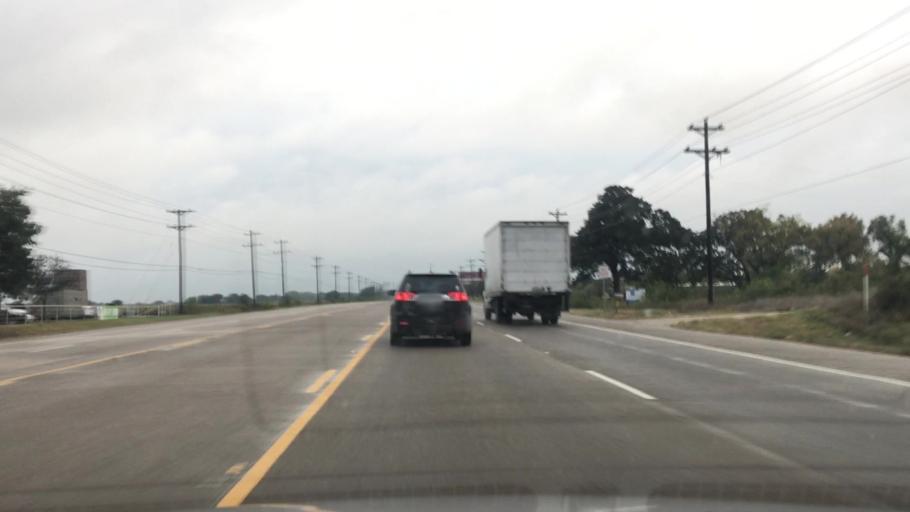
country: US
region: Texas
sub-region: Denton County
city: Cross Roads
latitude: 33.2217
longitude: -96.9553
